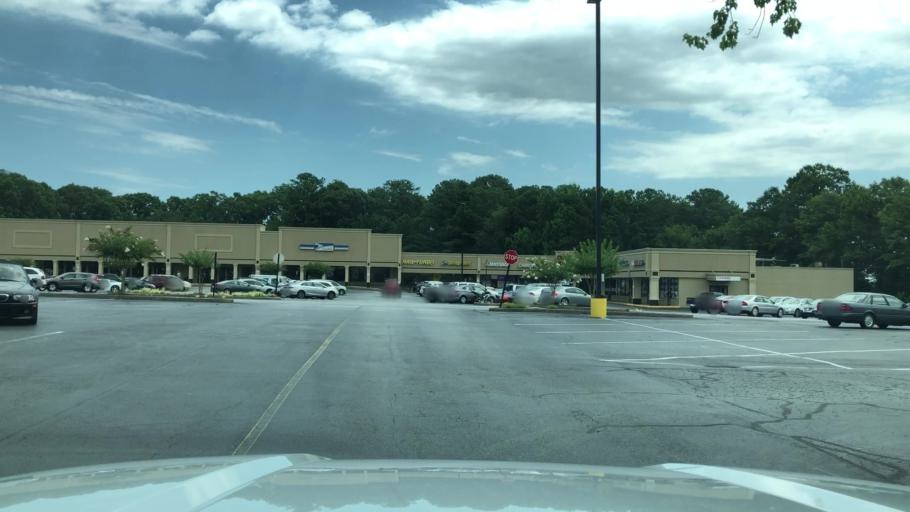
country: US
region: Georgia
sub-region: Fulton County
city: Roswell
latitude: 34.0399
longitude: -84.3420
